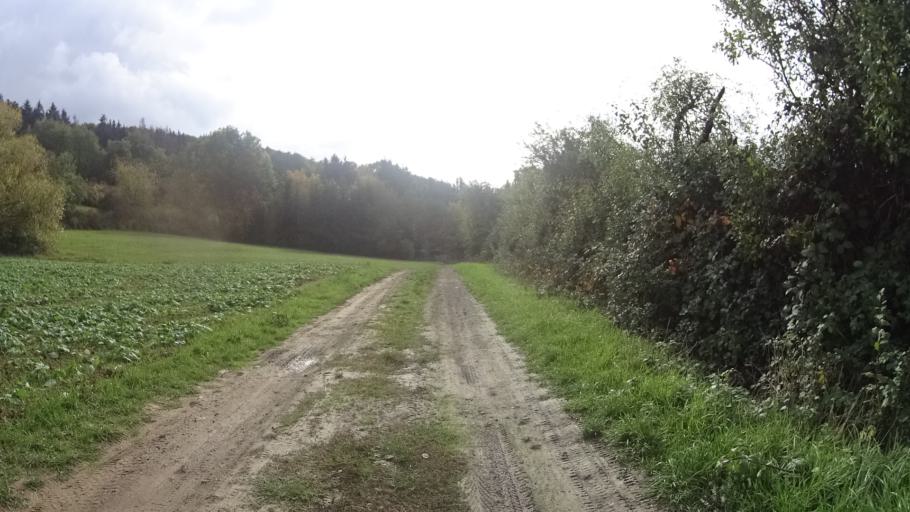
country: DE
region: Rheinland-Pfalz
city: Rockenhausen
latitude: 49.6391
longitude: 7.8439
